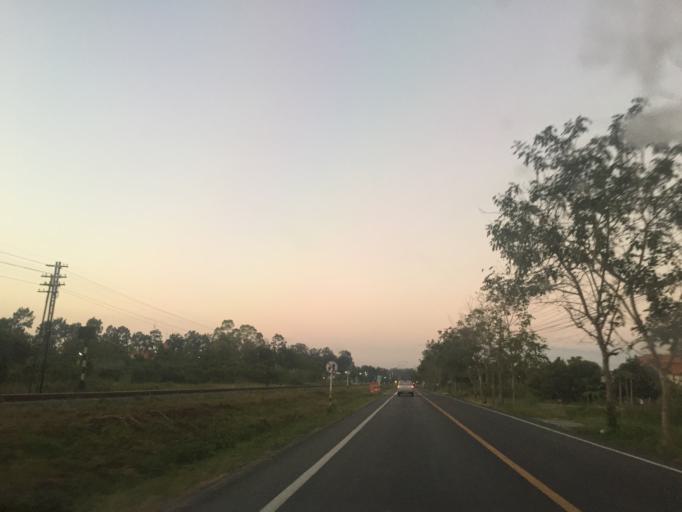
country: TH
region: Chiang Mai
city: Saraphi
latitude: 18.6750
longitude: 99.0446
